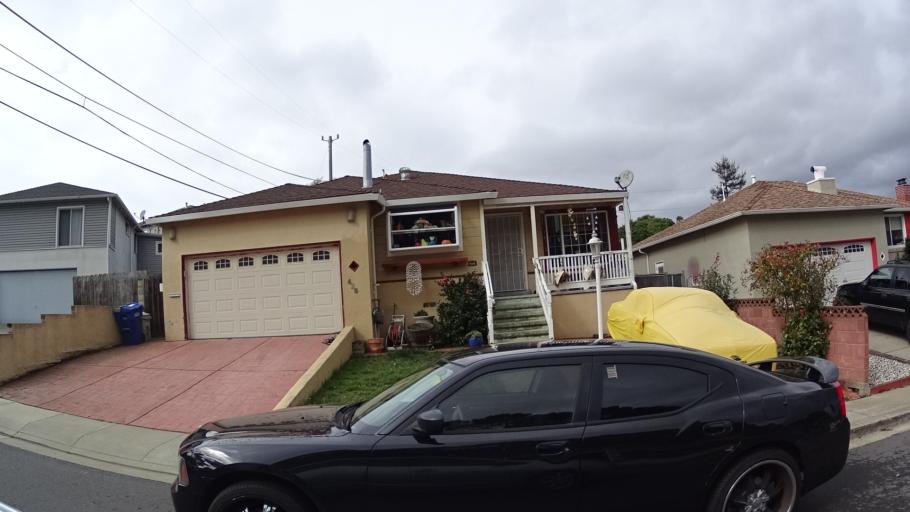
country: US
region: California
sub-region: San Mateo County
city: San Bruno
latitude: 37.6365
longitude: -122.4341
